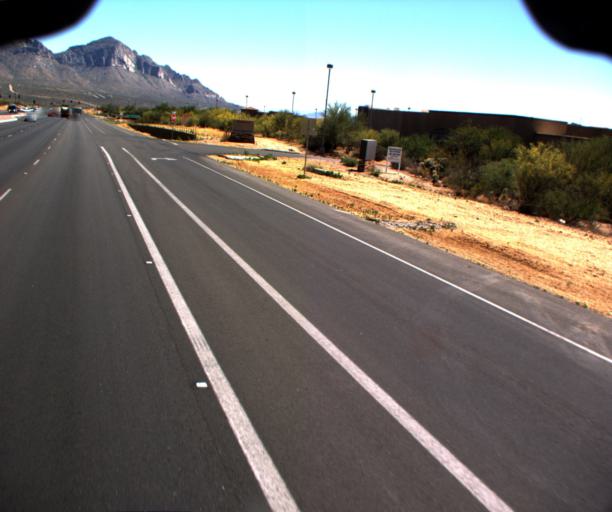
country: US
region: Arizona
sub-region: Pima County
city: Oro Valley
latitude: 32.4431
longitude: -110.9341
